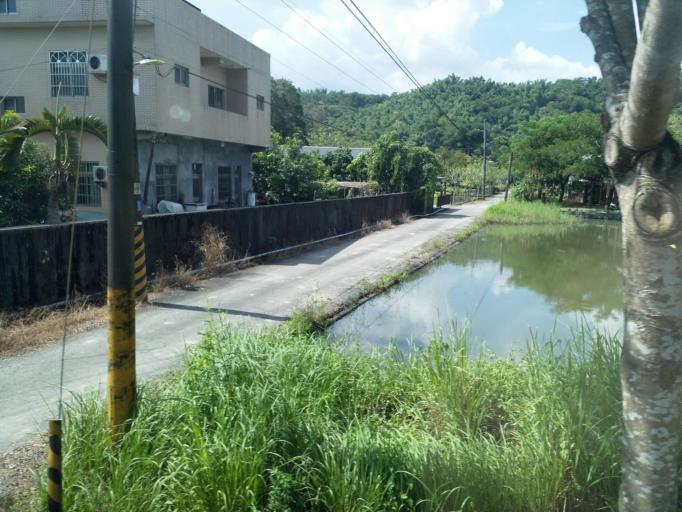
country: TW
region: Taiwan
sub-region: Pingtung
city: Pingtung
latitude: 22.9003
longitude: 120.5792
